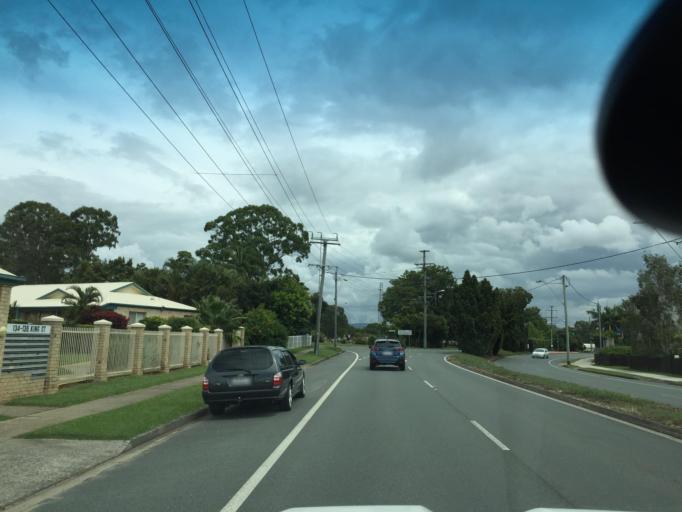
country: AU
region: Queensland
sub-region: Moreton Bay
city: Caboolture
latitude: -27.0853
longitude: 152.9423
